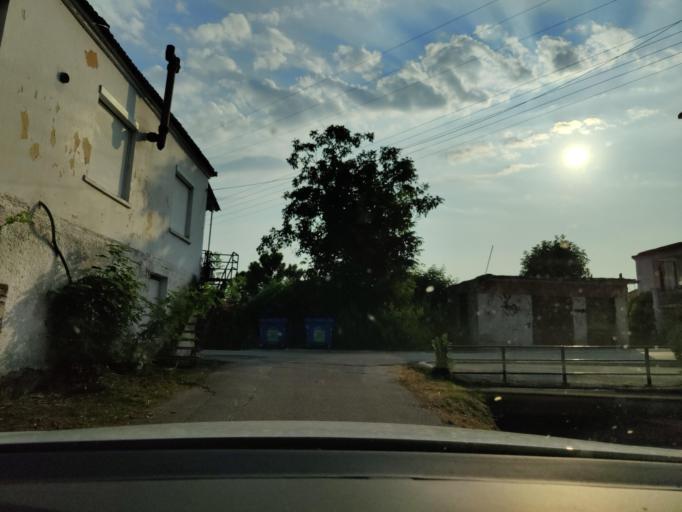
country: GR
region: East Macedonia and Thrace
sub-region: Nomos Kavalas
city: Zygos
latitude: 41.0171
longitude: 24.3827
